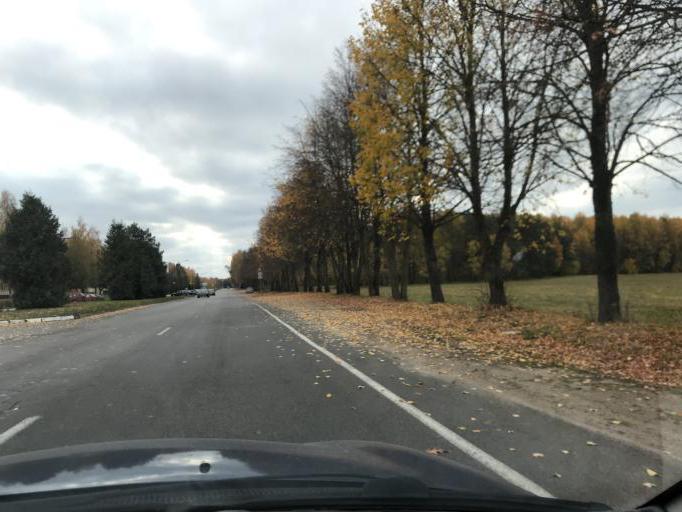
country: BY
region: Grodnenskaya
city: Lida
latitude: 53.9423
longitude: 25.2456
